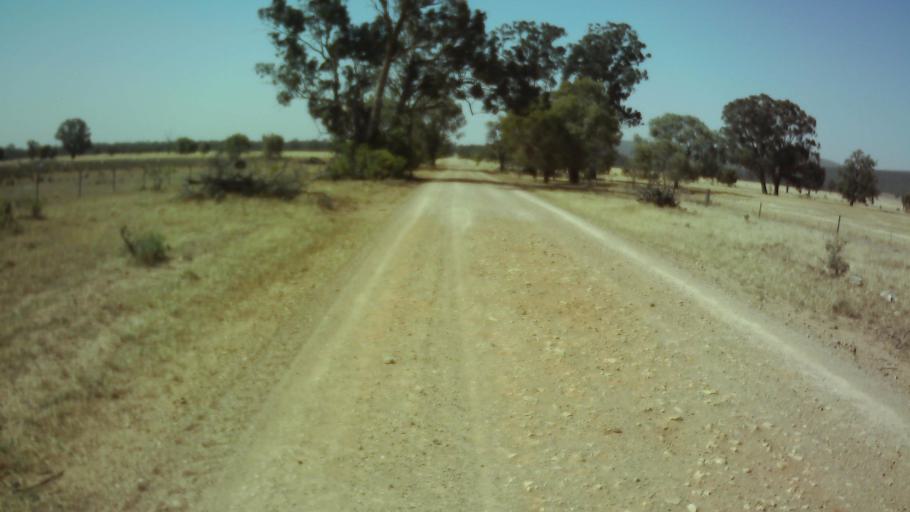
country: AU
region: New South Wales
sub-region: Weddin
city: Grenfell
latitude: -33.9875
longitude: 147.9271
